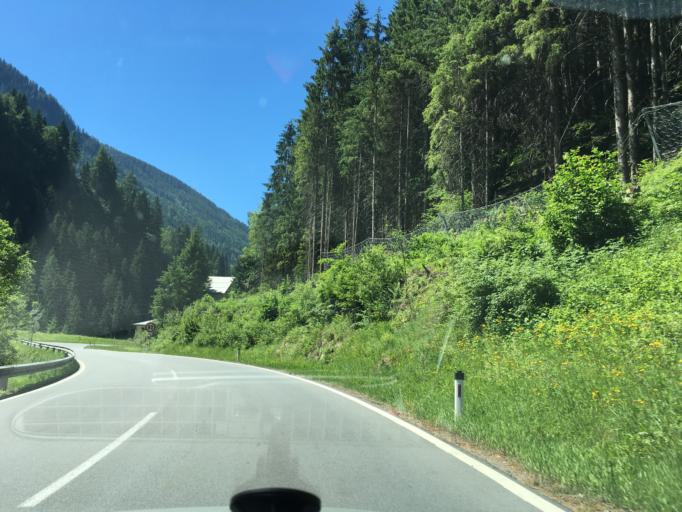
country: AT
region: Tyrol
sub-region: Politischer Bezirk Landeck
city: See
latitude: 47.1005
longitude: 10.4851
